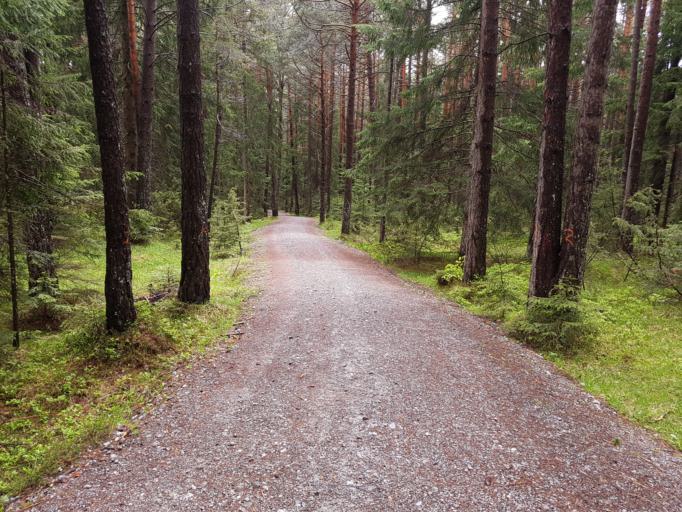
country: AT
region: Tyrol
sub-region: Politischer Bezirk Imst
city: Obsteig
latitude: 47.3058
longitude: 10.9048
